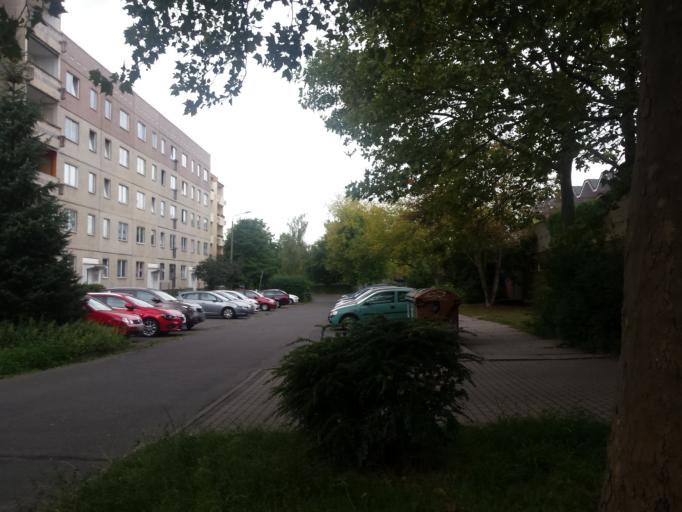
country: DE
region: Saxony
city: Taucha
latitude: 51.3549
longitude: 12.4569
